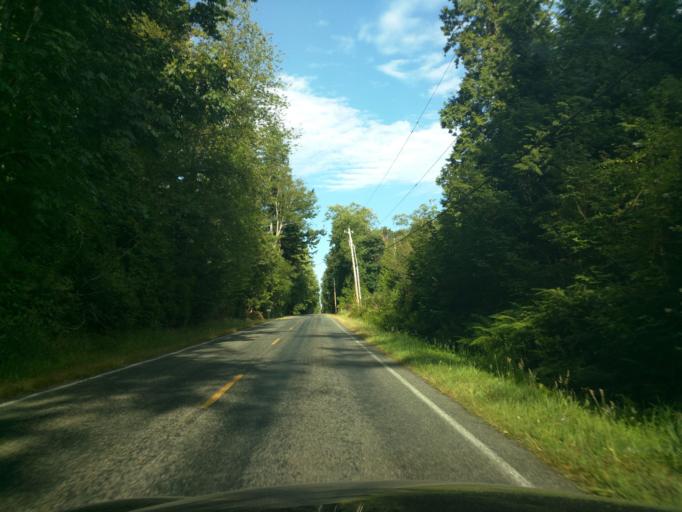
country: US
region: Washington
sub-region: Whatcom County
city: Blaine
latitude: 48.9939
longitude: -122.6948
